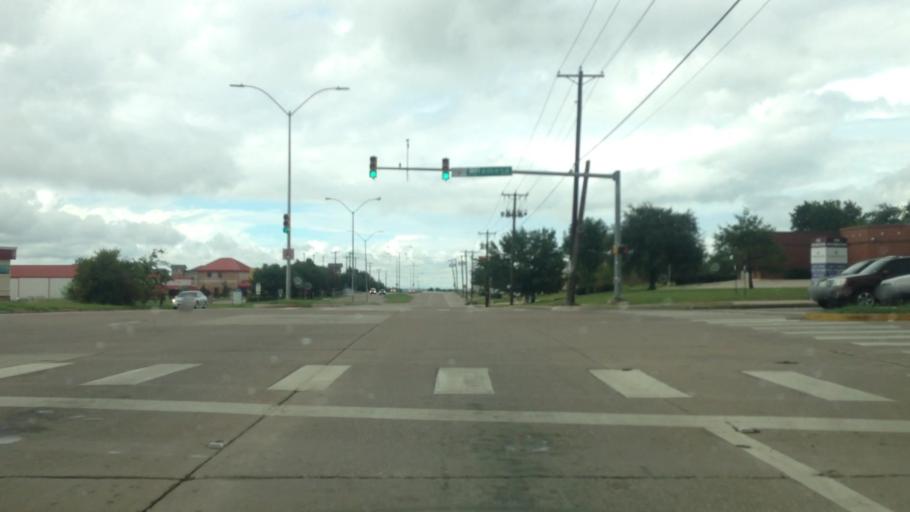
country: US
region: Texas
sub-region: Tarrant County
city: Benbrook
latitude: 32.6438
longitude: -97.4096
